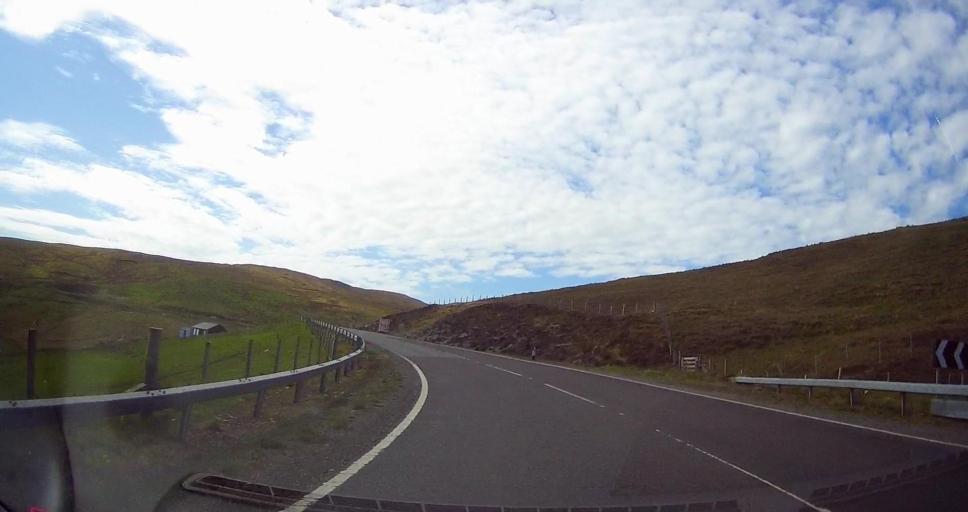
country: GB
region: Scotland
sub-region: Shetland Islands
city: Sandwick
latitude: 59.9906
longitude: -1.2836
